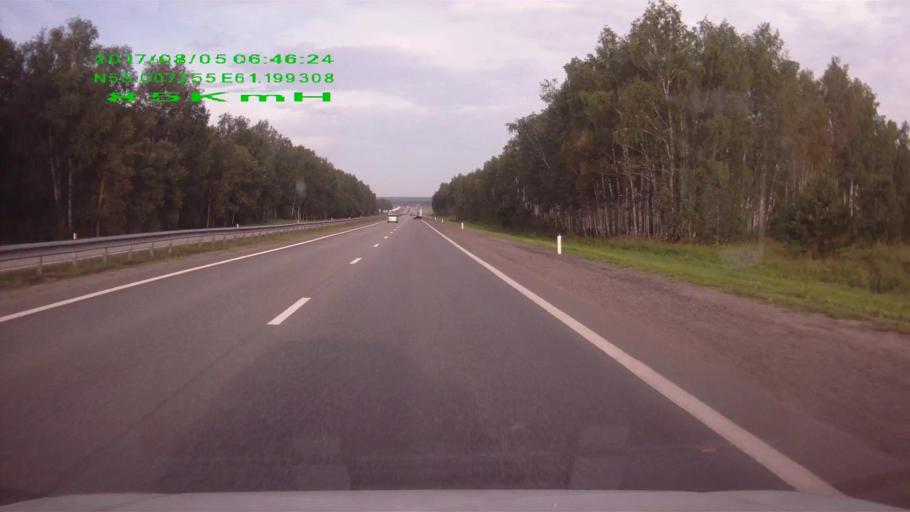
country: RU
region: Chelyabinsk
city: Sargazy
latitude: 55.0072
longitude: 61.1991
